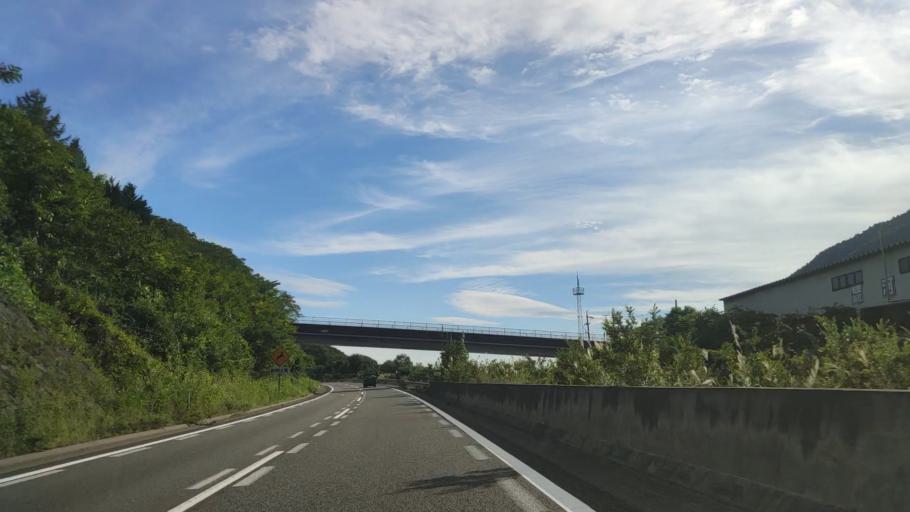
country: JP
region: Nagano
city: Tatsuno
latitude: 36.0053
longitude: 138.0084
